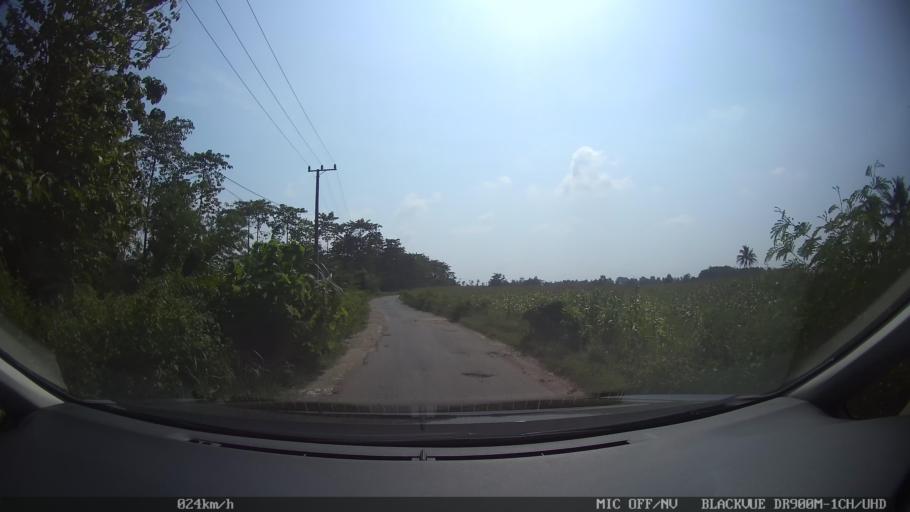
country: ID
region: Lampung
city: Natar
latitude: -5.2659
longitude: 105.2004
